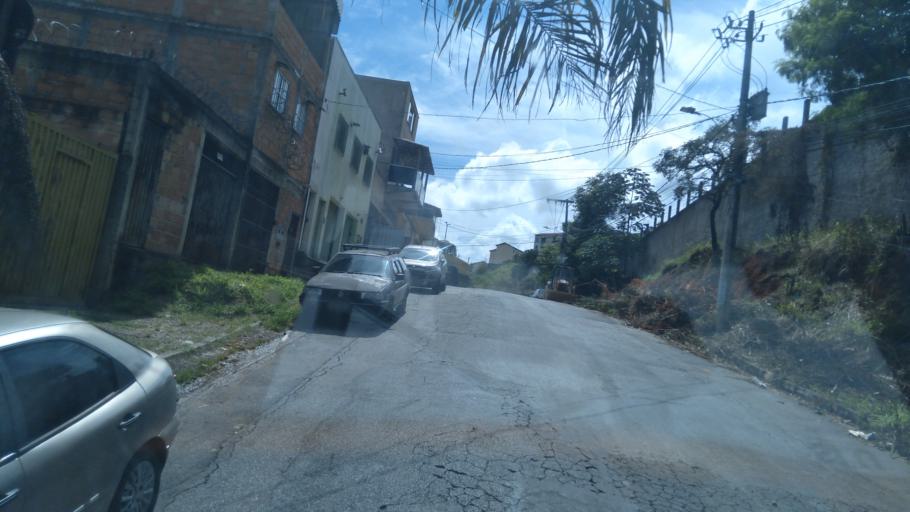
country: BR
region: Minas Gerais
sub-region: Belo Horizonte
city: Belo Horizonte
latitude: -19.8597
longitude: -43.8940
